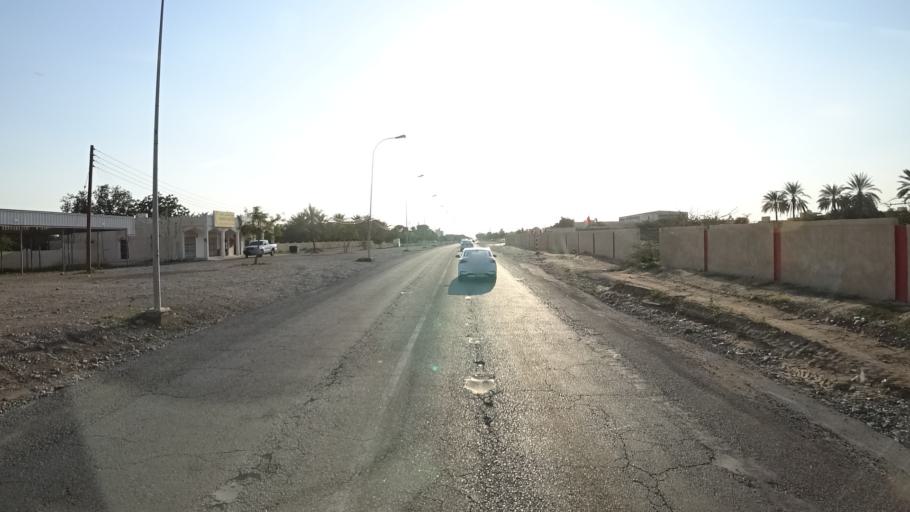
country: OM
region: Al Batinah
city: Al Khaburah
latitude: 23.9699
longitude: 57.0893
